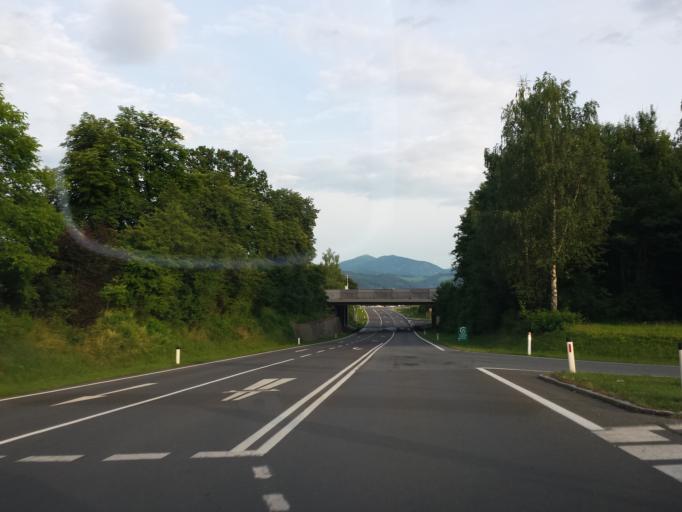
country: AT
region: Styria
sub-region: Politischer Bezirk Murtal
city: Spielberg bei Knittelfeld
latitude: 47.2124
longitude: 14.7845
